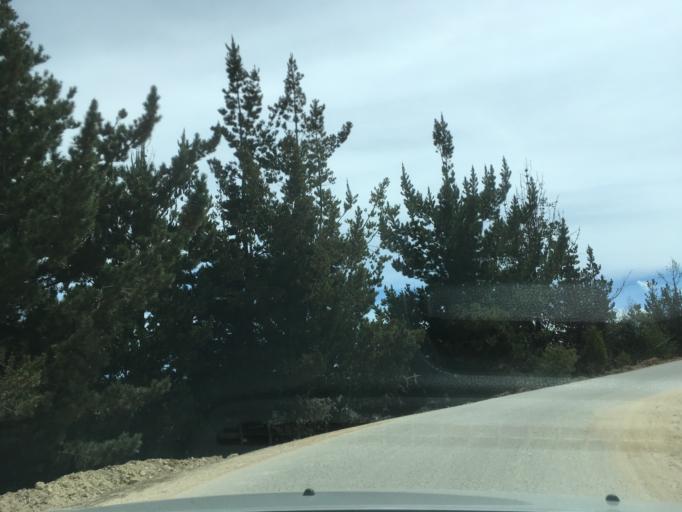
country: CO
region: Boyaca
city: Aquitania
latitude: 5.5847
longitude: -72.9243
